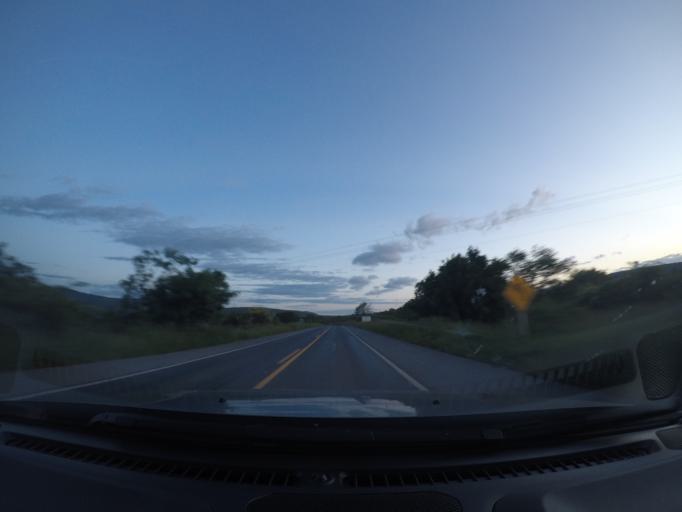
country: BR
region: Bahia
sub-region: Seabra
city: Seabra
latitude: -12.4804
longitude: -41.7390
